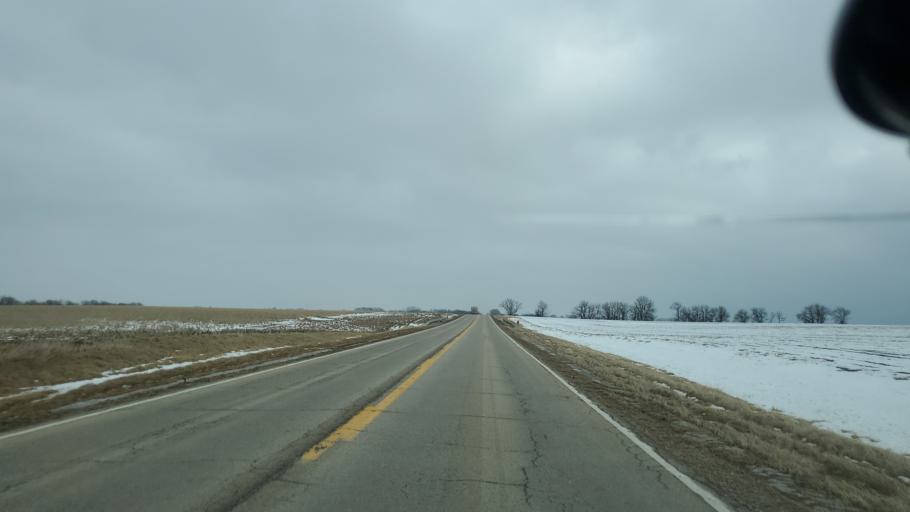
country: US
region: Illinois
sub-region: Marshall County
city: Toluca
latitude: 41.1186
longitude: -89.1768
